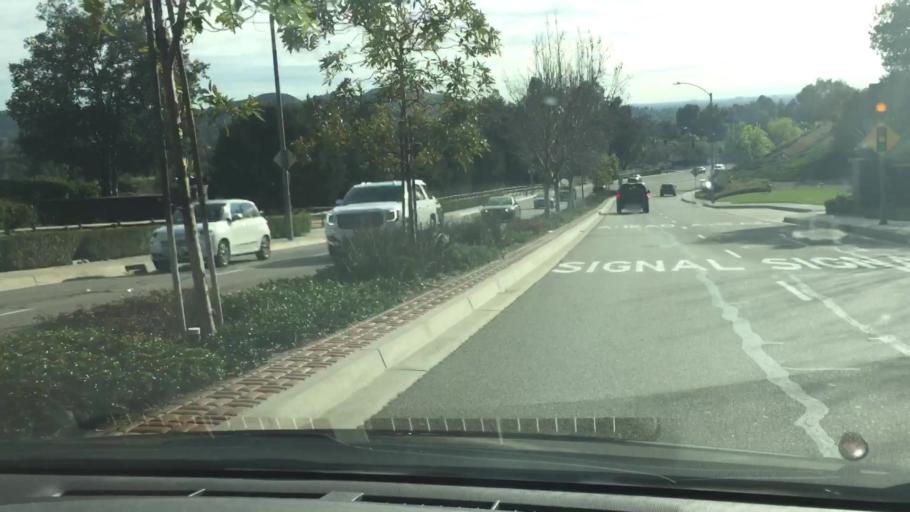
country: US
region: California
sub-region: Orange County
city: Villa Park
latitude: 33.8238
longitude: -117.7819
